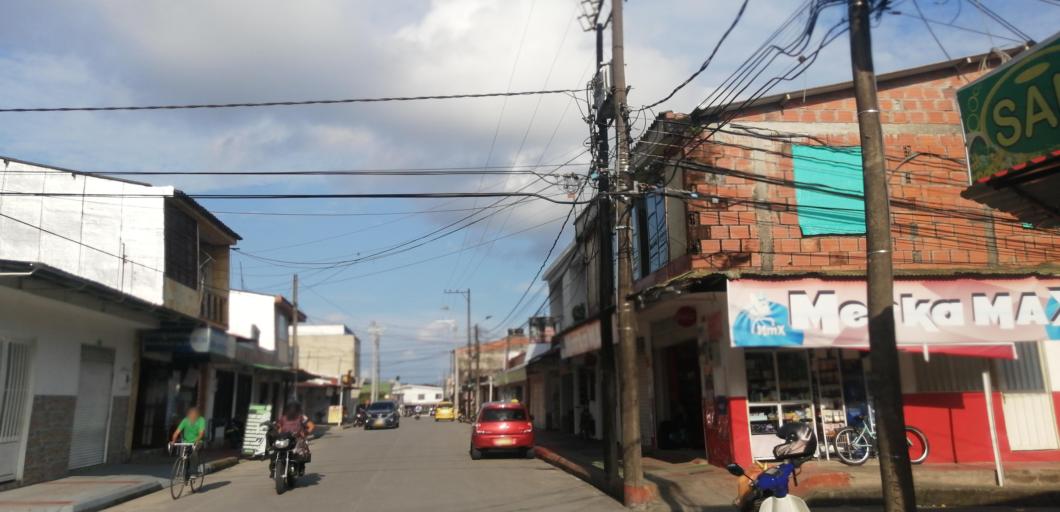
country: CO
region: Meta
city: Acacias
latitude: 3.9856
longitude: -73.7767
